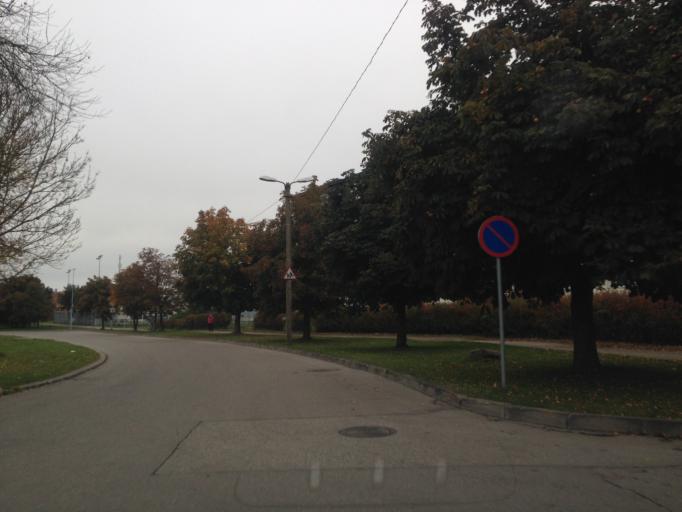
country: EE
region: Harju
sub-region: Harku vald
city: Tabasalu
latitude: 59.4272
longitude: 24.5386
